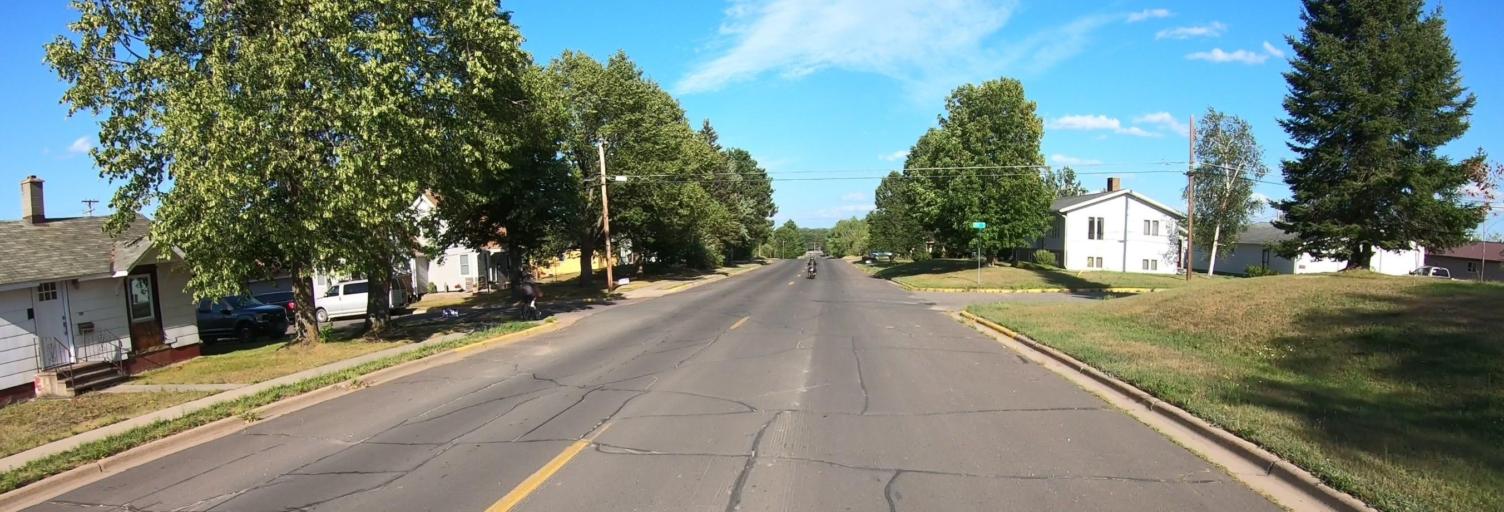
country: US
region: Minnesota
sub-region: Saint Louis County
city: Ely
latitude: 47.9012
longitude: -91.8523
